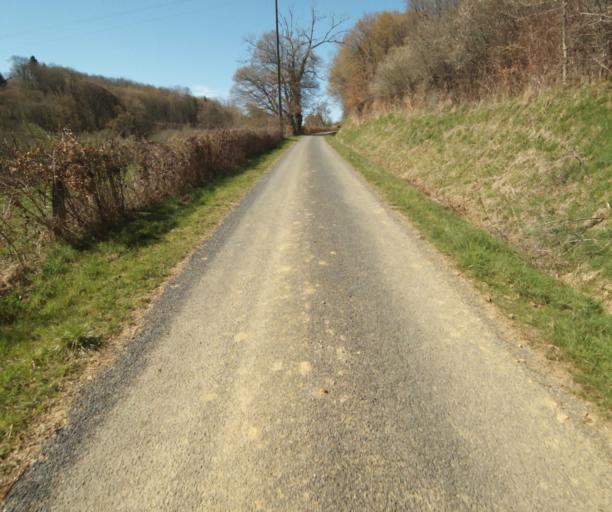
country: FR
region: Limousin
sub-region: Departement de la Correze
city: Chamboulive
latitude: 45.4590
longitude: 1.6754
